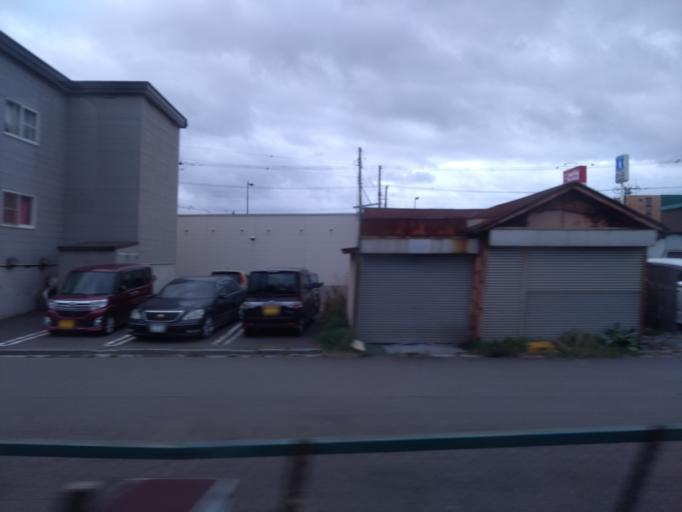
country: JP
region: Hokkaido
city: Hakodate
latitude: 41.7862
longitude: 140.7297
